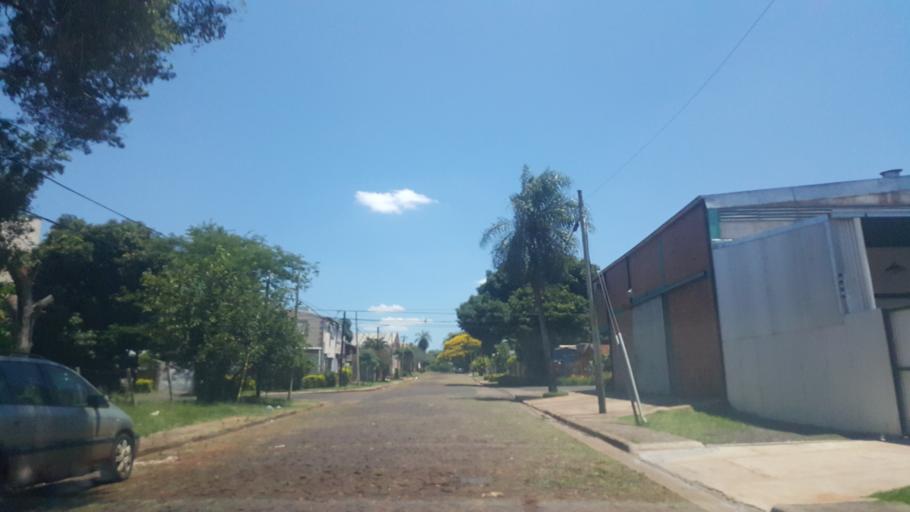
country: AR
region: Misiones
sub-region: Departamento de Capital
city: Posadas
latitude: -27.3881
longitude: -55.9053
